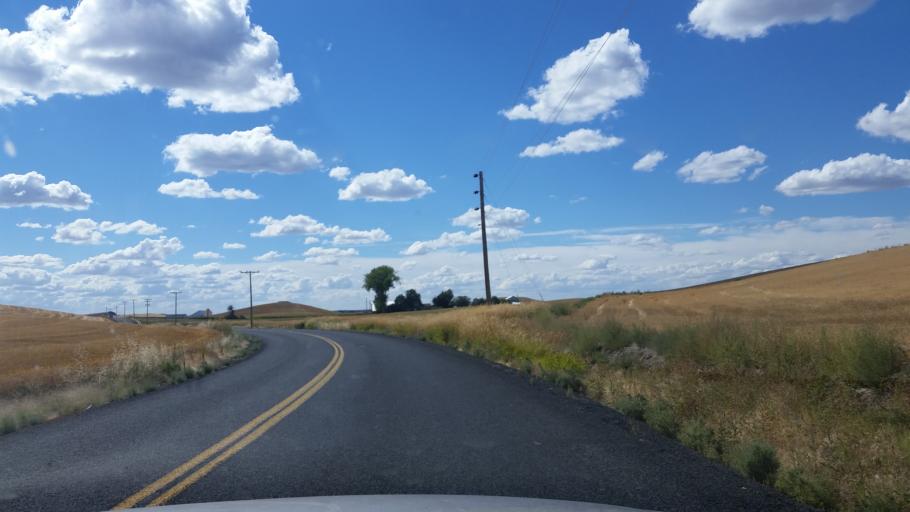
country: US
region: Washington
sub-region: Spokane County
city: Cheney
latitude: 47.3836
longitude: -117.4896
